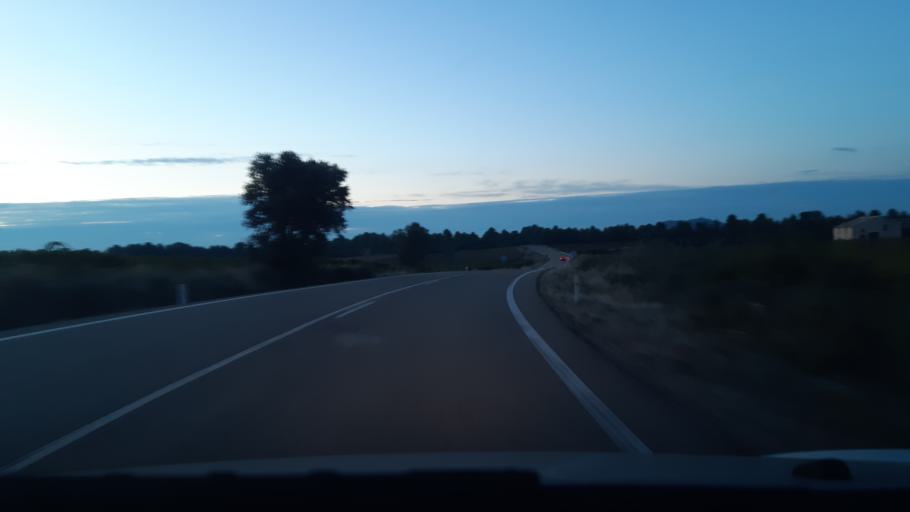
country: ES
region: Aragon
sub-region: Provincia de Teruel
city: Lledo
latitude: 40.9588
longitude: 0.2152
